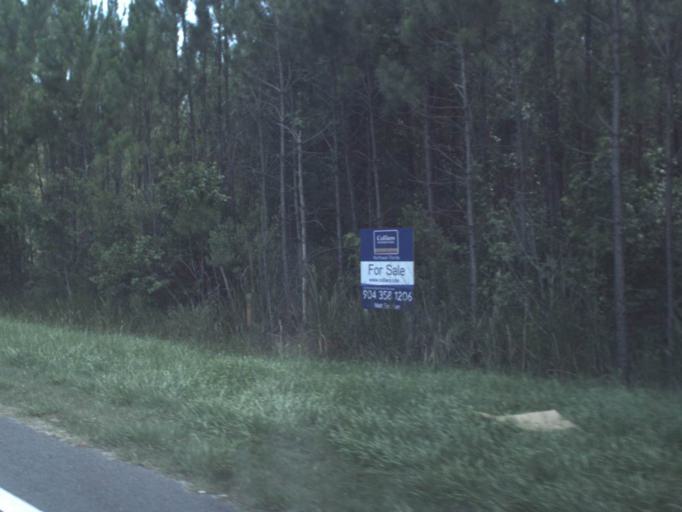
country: US
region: Florida
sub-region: Nassau County
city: Yulee
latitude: 30.6251
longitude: -81.5995
